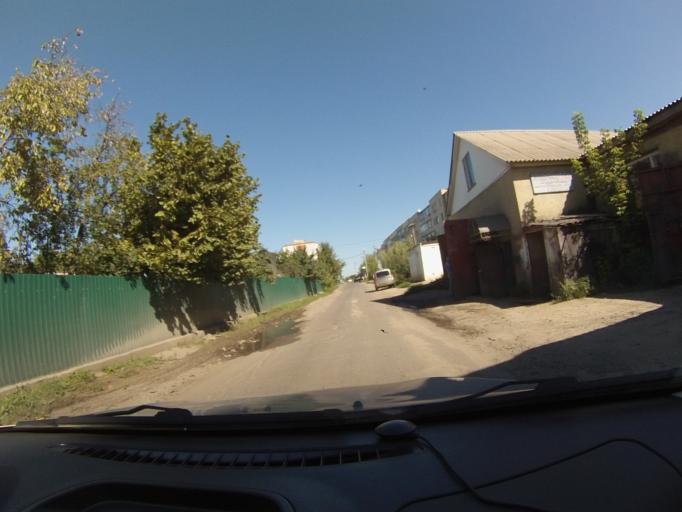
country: RU
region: Tambov
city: Donskoye
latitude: 52.7628
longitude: 41.4715
